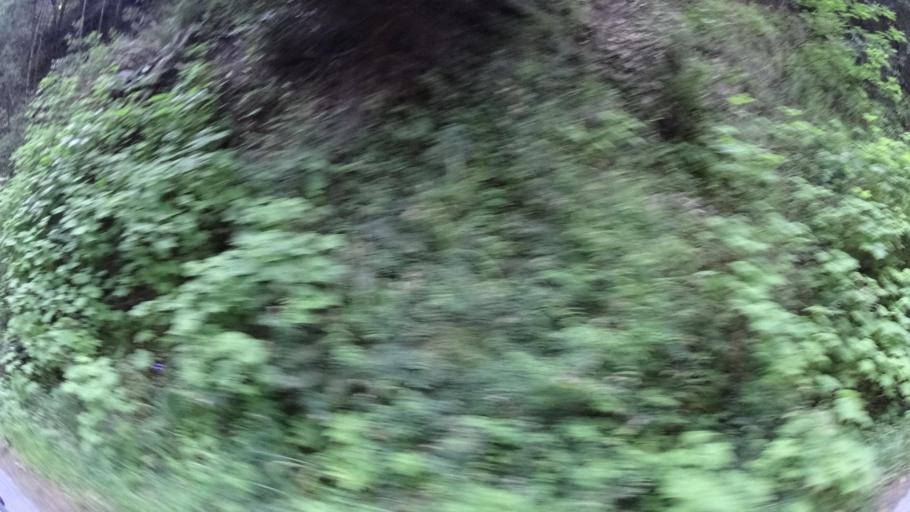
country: US
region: California
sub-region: Humboldt County
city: Rio Dell
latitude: 40.4529
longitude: -123.9804
